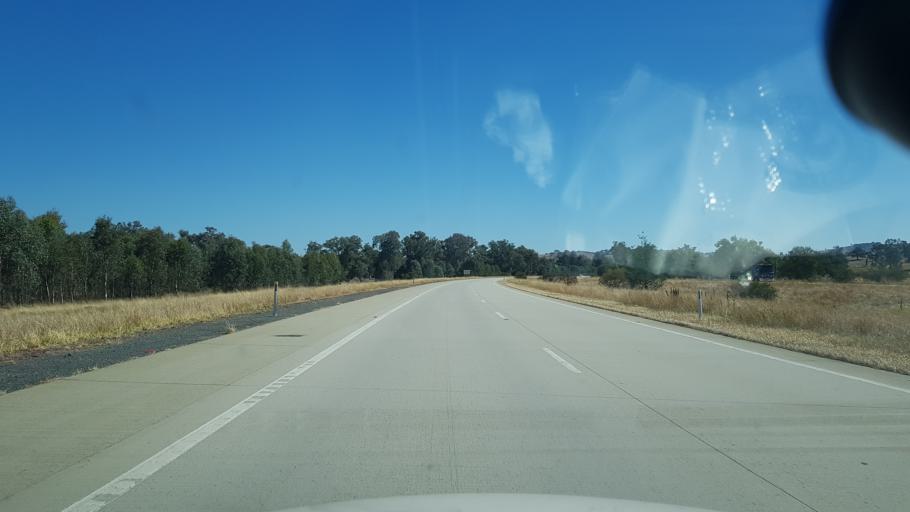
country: AU
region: New South Wales
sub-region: Greater Hume Shire
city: Holbrook
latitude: -35.9133
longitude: 147.1518
